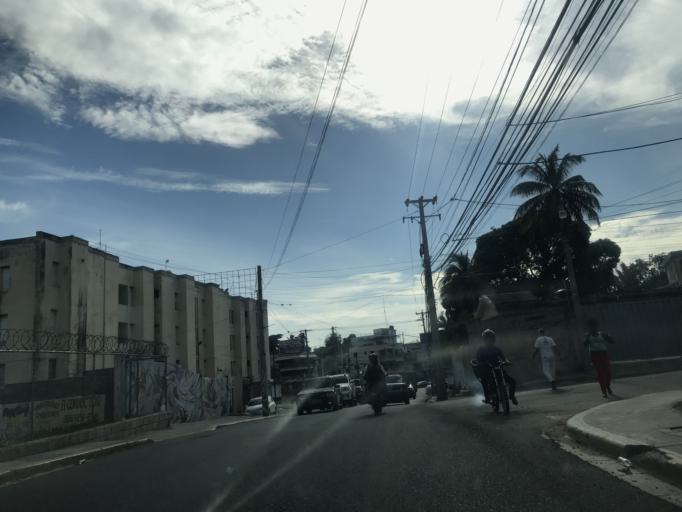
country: DO
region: Santiago
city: Santiago de los Caballeros
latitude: 19.4284
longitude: -70.6867
